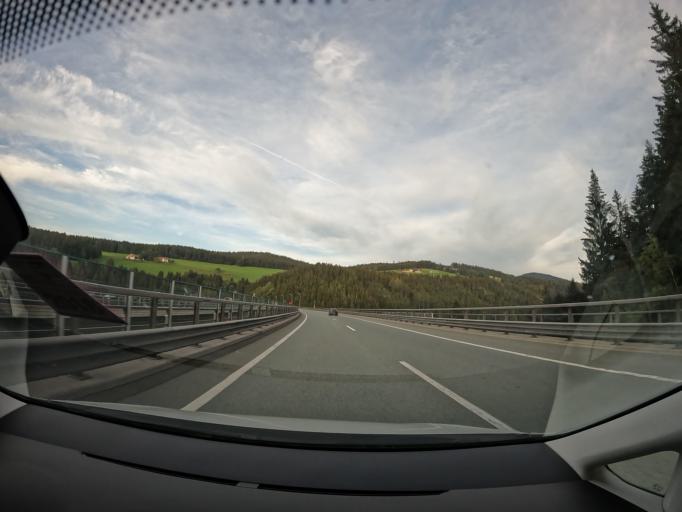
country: AT
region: Styria
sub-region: Politischer Bezirk Voitsberg
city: Pack
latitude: 46.9171
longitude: 14.9927
